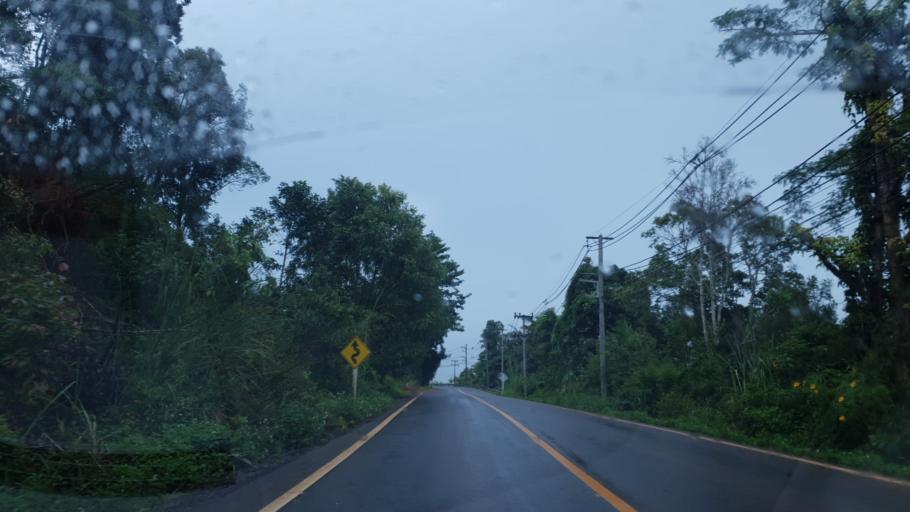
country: TH
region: Mae Hong Son
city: Ban Huai I Huak
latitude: 18.1355
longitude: 98.0774
